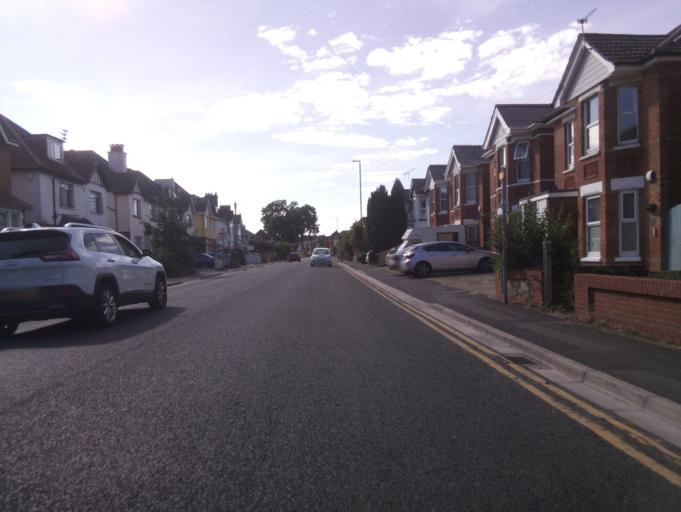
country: GB
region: England
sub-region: Bournemouth
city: Bournemouth
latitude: 50.7406
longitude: -1.8817
